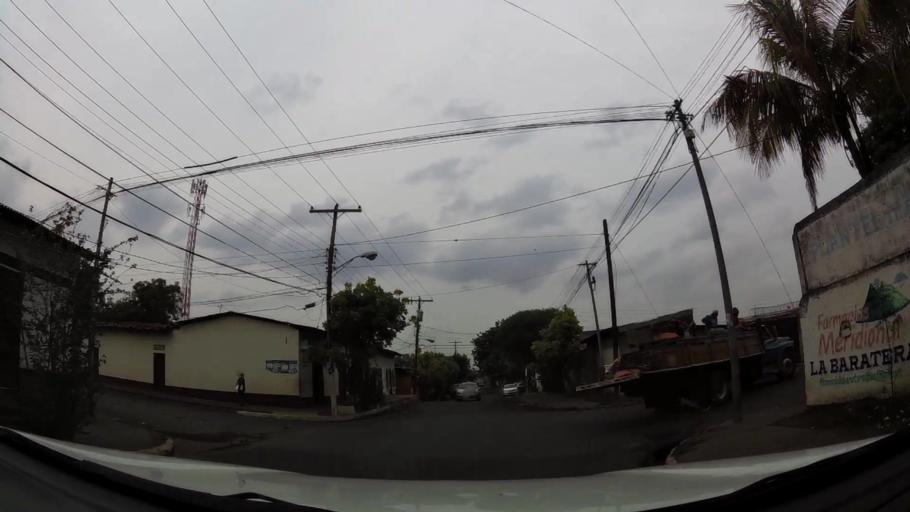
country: NI
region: Leon
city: Leon
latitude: 12.4454
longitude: -86.8798
